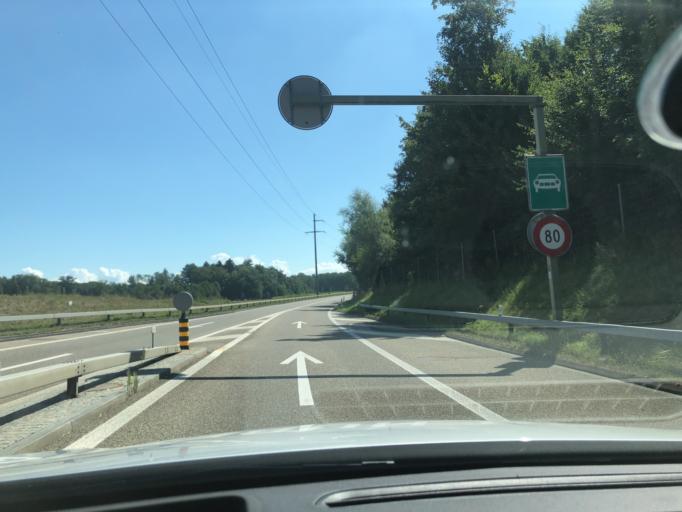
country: CH
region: Thurgau
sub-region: Kreuzlingen District
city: Tagerwilen
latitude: 47.6345
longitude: 9.1473
